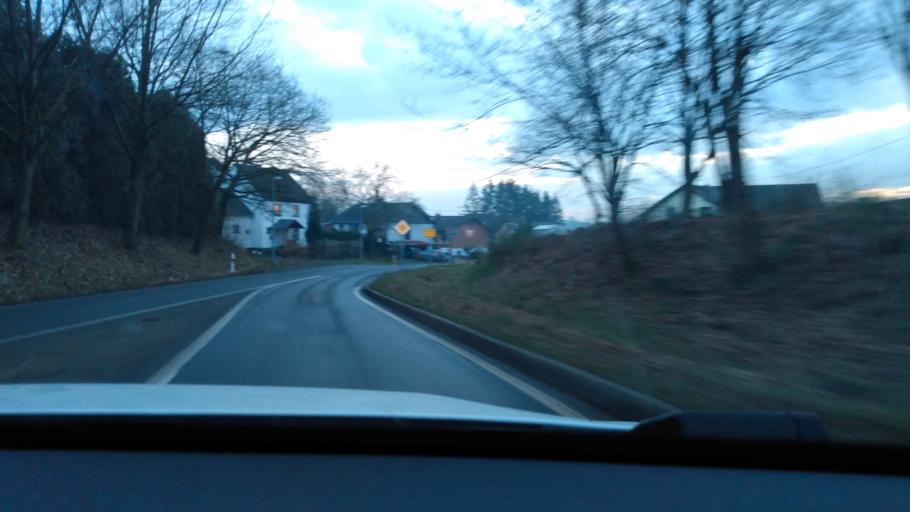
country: DE
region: Rheinland-Pfalz
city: Kircheib
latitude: 50.7013
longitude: 7.4349
